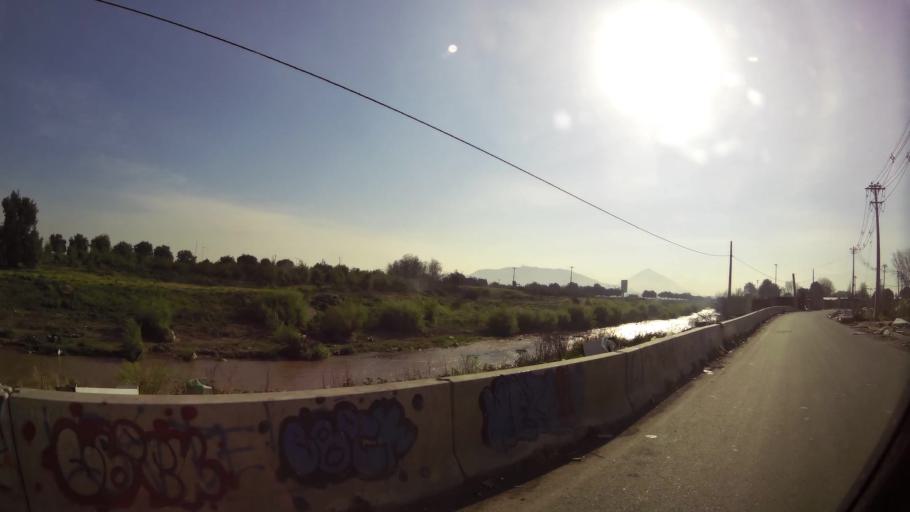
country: CL
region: Santiago Metropolitan
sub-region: Provincia de Santiago
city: Lo Prado
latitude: -33.4149
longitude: -70.7704
